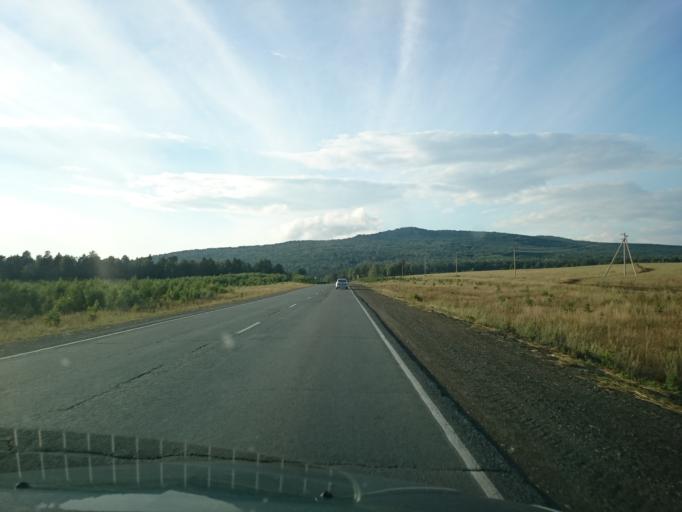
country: RU
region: Bashkortostan
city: Lomovka
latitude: 53.8907
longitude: 58.0952
